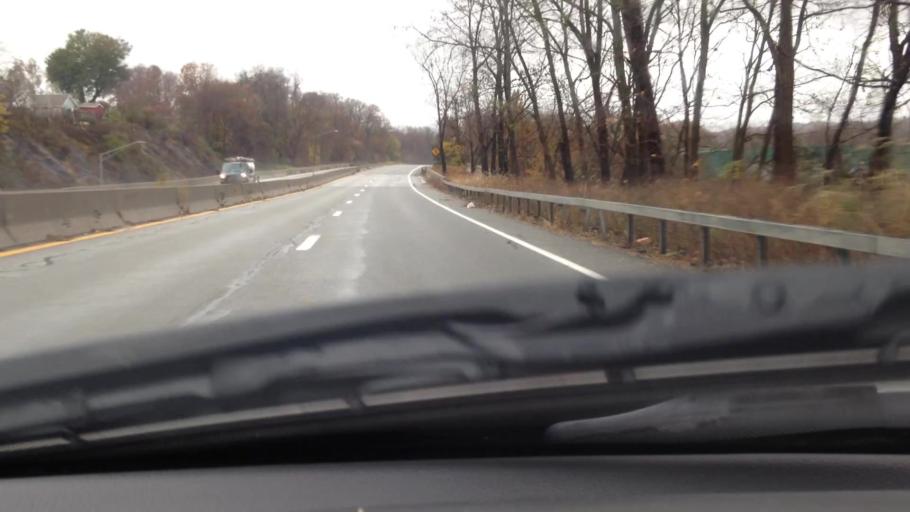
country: US
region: New York
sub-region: Westchester County
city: Peekskill
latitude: 41.2779
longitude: -73.9307
